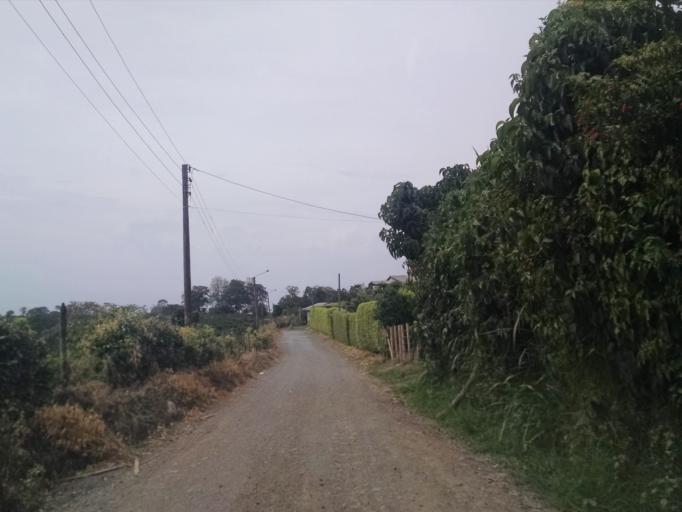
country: CO
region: Valle del Cauca
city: Ulloa
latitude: 4.7179
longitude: -75.7182
